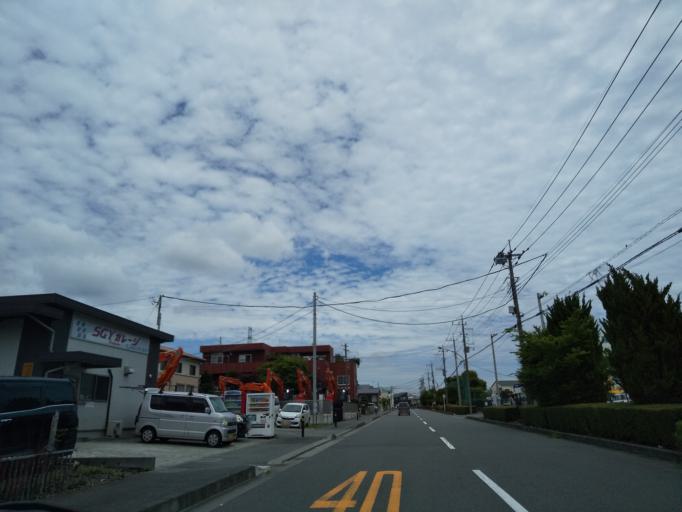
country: JP
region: Kanagawa
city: Zama
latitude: 35.5201
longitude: 139.3390
